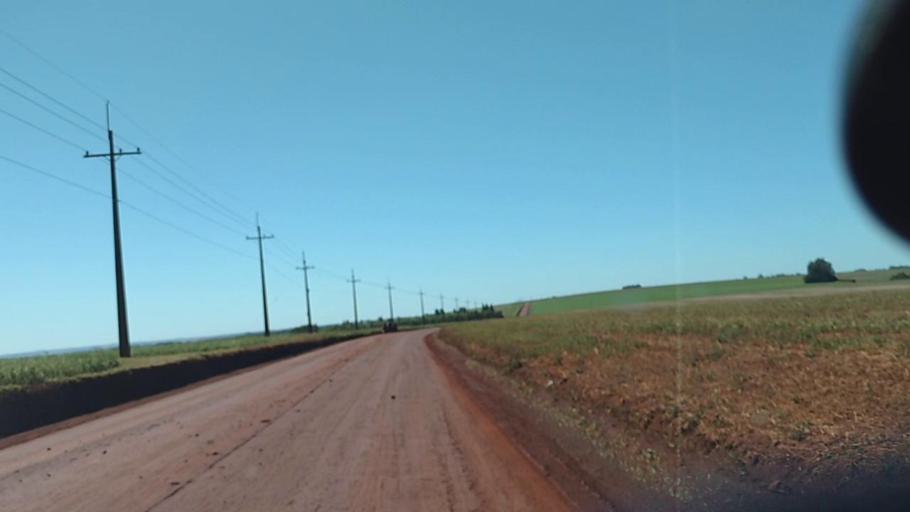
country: PY
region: Alto Parana
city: Naranjal
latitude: -25.9410
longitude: -55.2888
